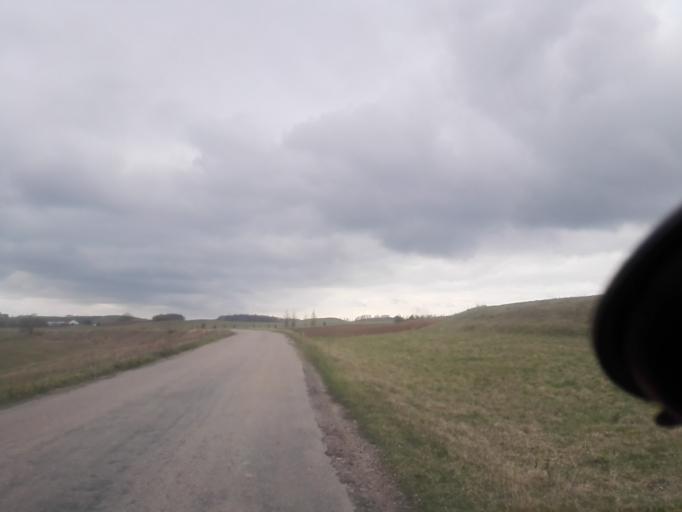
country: PL
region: Podlasie
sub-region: Suwalki
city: Suwalki
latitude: 54.2410
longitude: 22.9780
